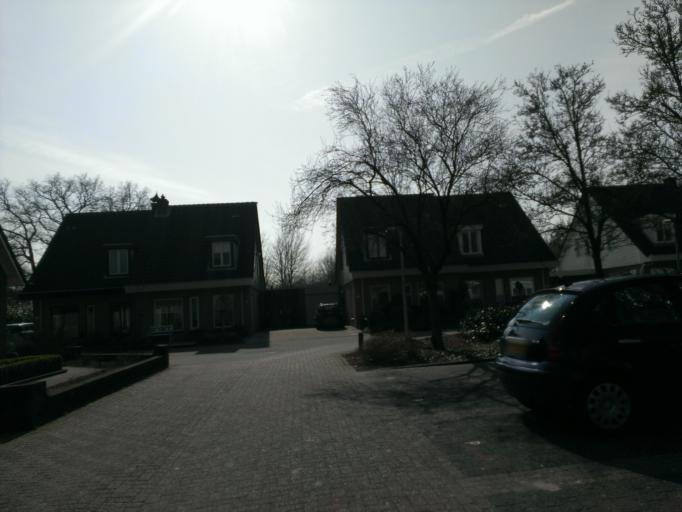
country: NL
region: Gelderland
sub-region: Gemeente Voorst
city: Twello
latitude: 52.2276
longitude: 6.1056
